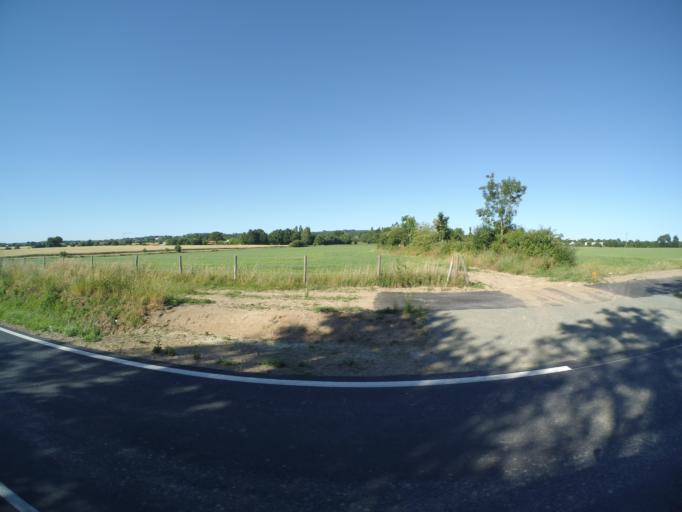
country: FR
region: Pays de la Loire
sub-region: Departement de la Vendee
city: Les Herbiers
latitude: 46.8793
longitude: -1.0319
